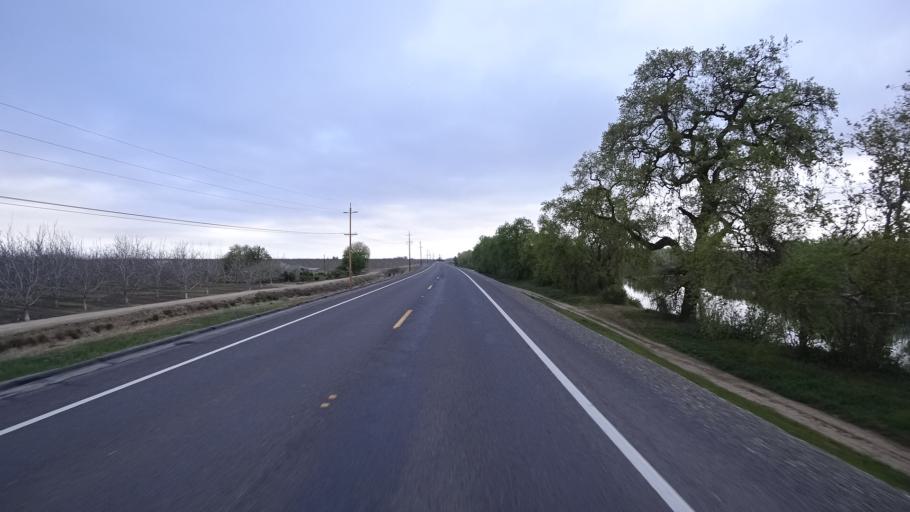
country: US
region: California
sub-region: Colusa County
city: Colusa
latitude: 39.4159
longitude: -122.0105
